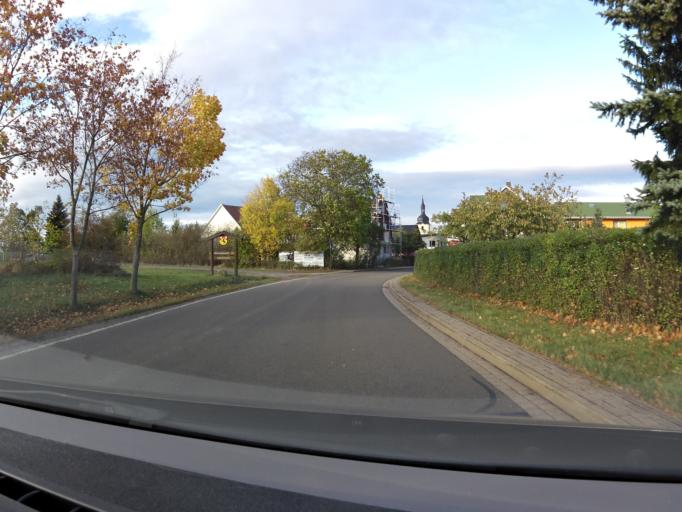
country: DE
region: Thuringia
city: Crawinkel
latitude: 50.7791
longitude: 10.7893
